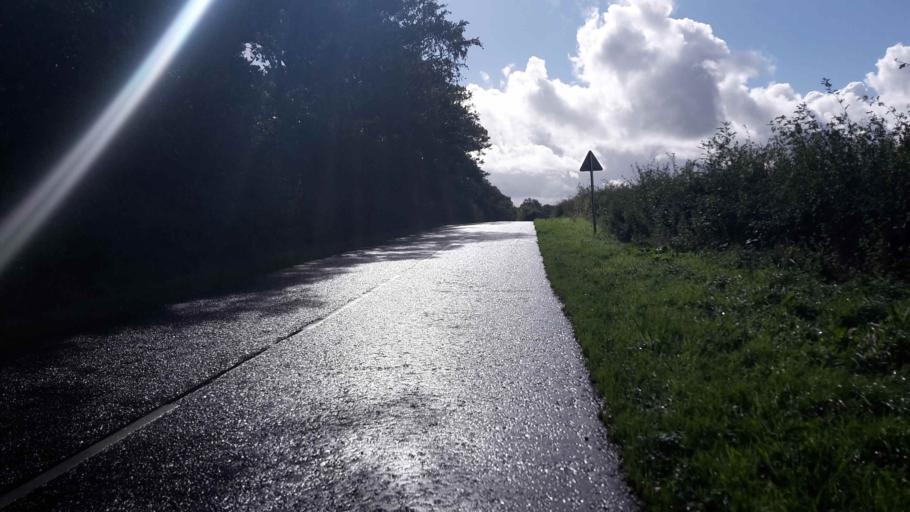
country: GB
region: Scotland
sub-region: South Lanarkshire
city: Carluke
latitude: 55.7286
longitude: -3.8543
